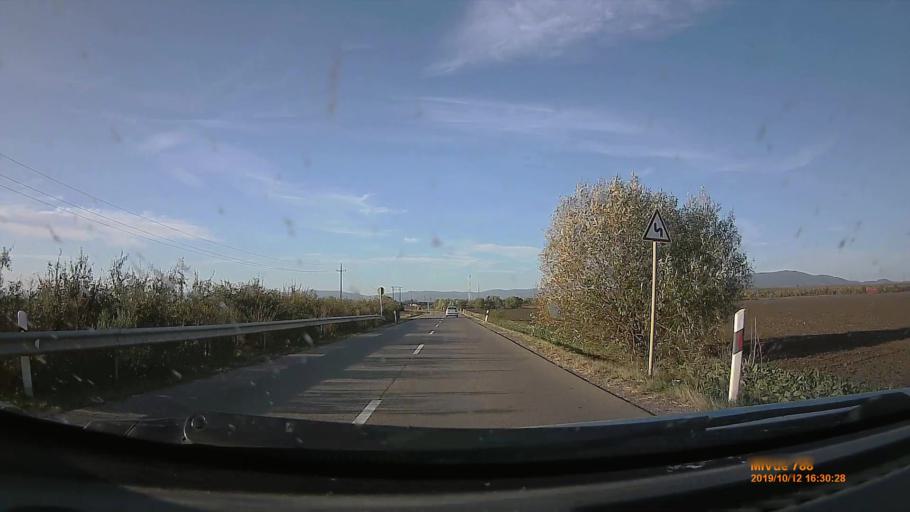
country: HU
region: Heves
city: Adacs
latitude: 47.7261
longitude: 19.9625
